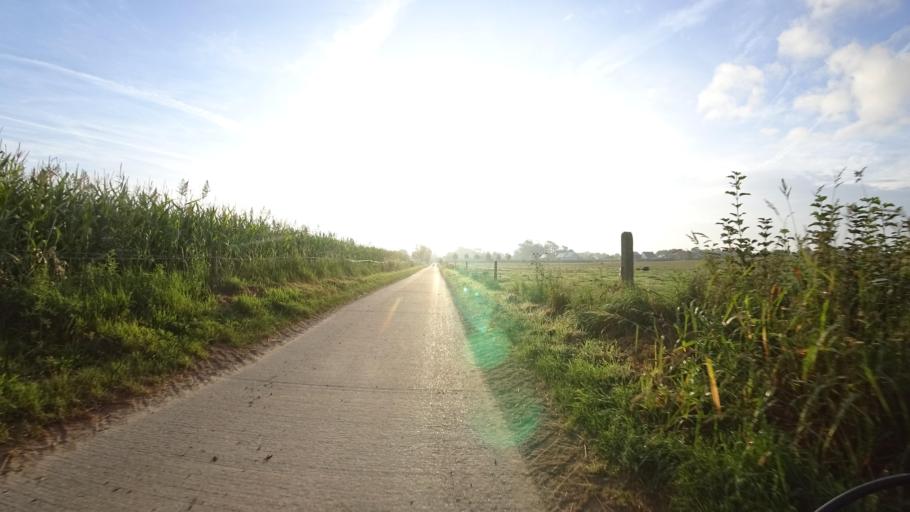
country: BE
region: Wallonia
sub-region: Province du Brabant Wallon
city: Walhain-Saint-Paul
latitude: 50.6234
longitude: 4.6873
